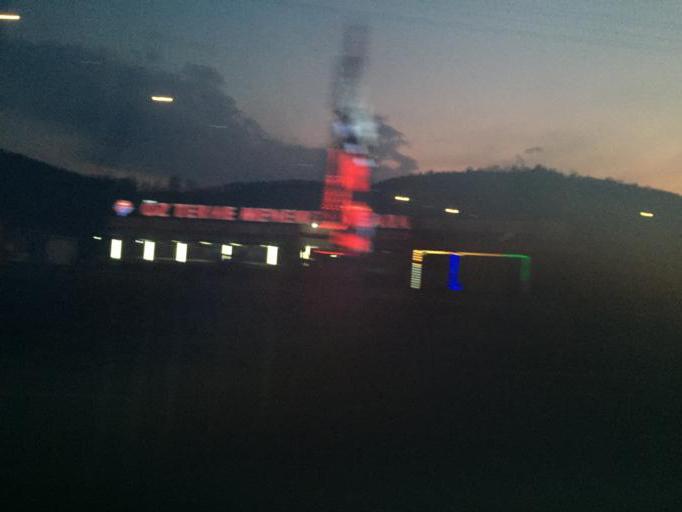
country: TR
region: Samsun
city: Kavak
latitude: 41.1366
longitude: 36.1256
